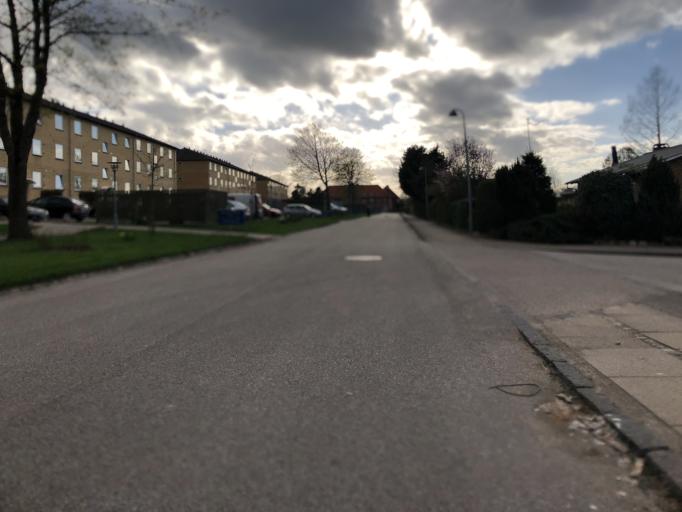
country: DK
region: Zealand
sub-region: Ringsted Kommune
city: Ringsted
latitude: 55.4444
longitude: 11.8064
